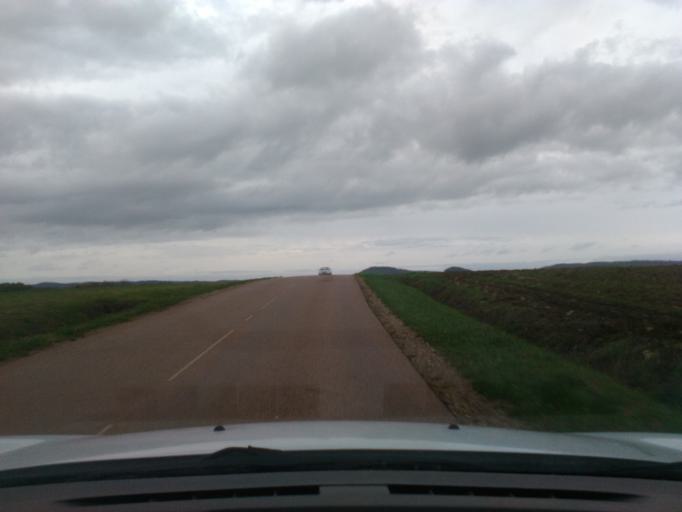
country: FR
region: Lorraine
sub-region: Departement des Vosges
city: Mirecourt
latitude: 48.3412
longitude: 6.1087
